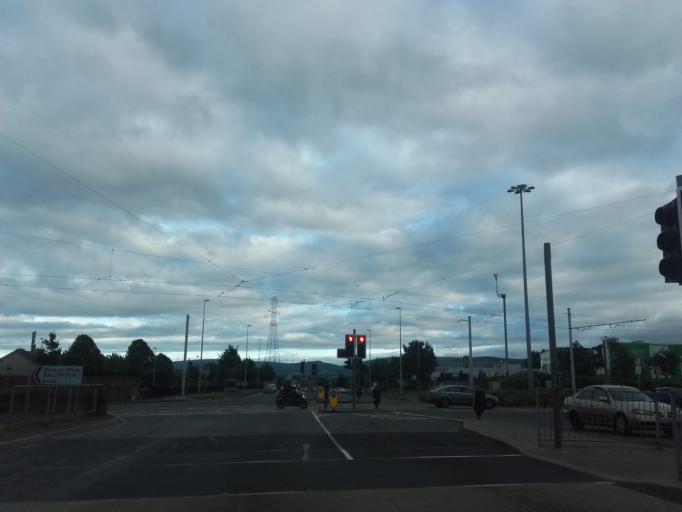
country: IE
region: Leinster
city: Tallaght
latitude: 53.3007
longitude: -6.3737
